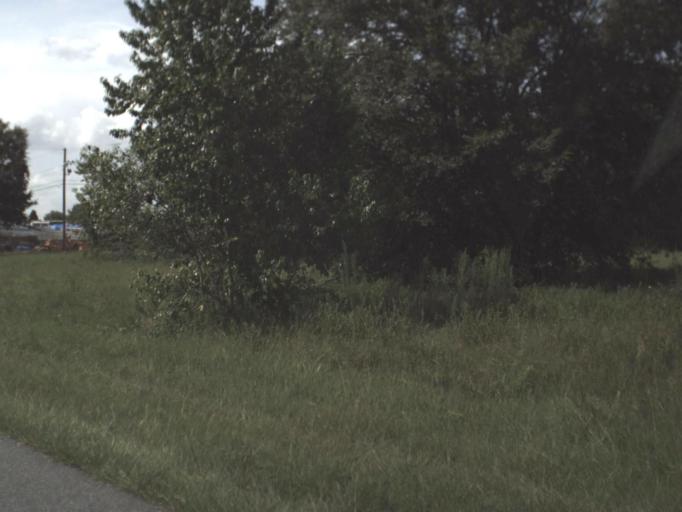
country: US
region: Florida
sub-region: Citrus County
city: Citrus Springs
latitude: 28.9712
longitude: -82.4216
